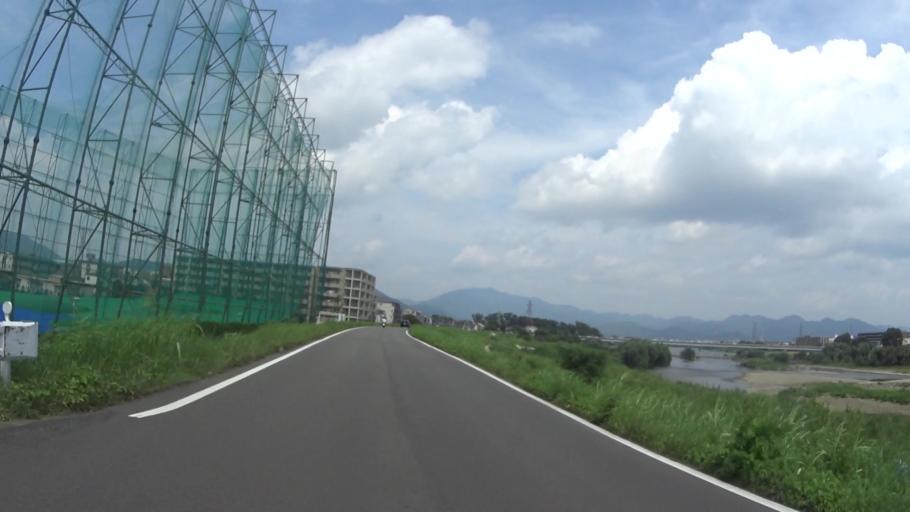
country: JP
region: Kyoto
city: Muko
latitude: 34.9780
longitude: 135.7156
